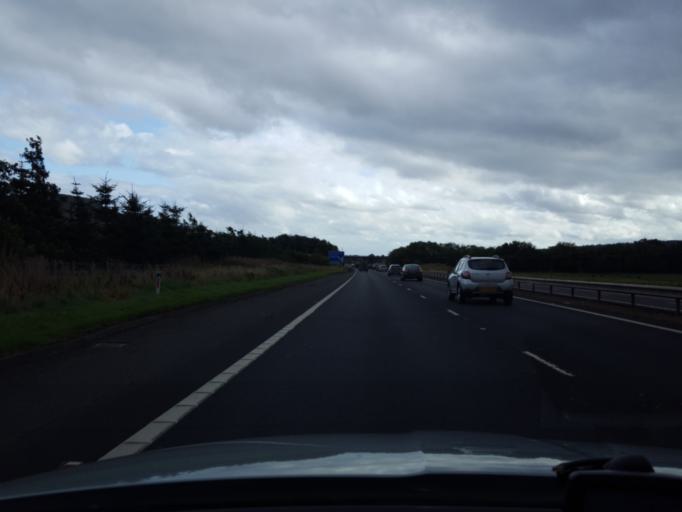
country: GB
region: Scotland
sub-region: Perth and Kinross
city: Kinross
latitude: 56.1807
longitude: -3.4142
